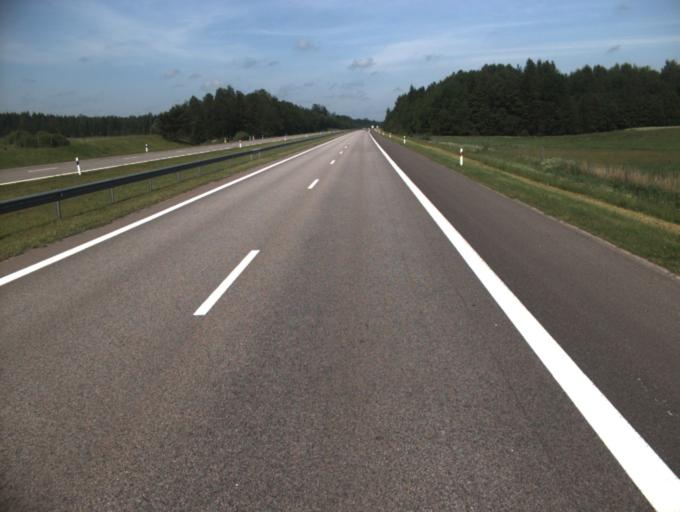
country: LT
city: Rietavas
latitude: 55.6623
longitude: 21.7556
